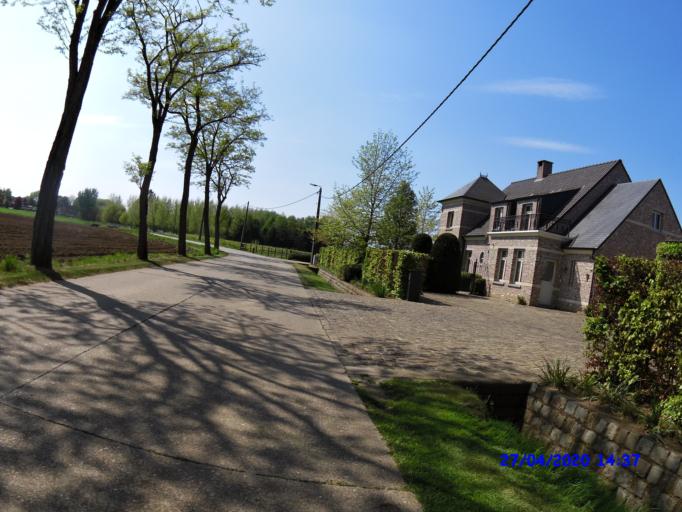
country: BE
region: Flanders
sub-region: Provincie Antwerpen
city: Lille
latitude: 51.2317
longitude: 4.8498
